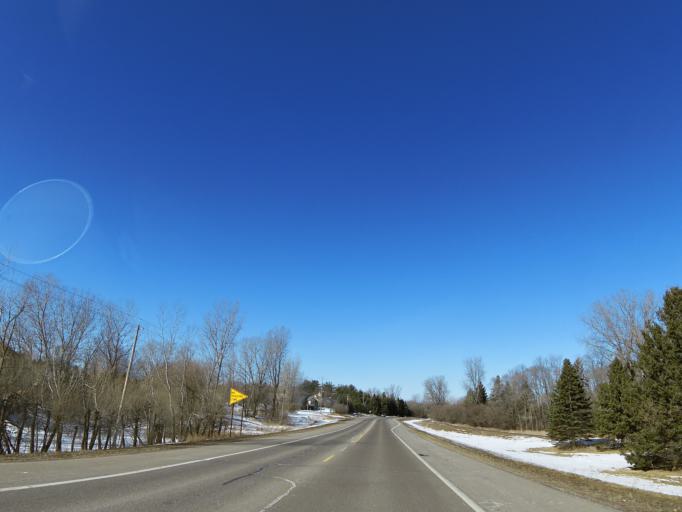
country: US
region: Minnesota
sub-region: Washington County
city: Stillwater
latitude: 45.0723
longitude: -92.8257
